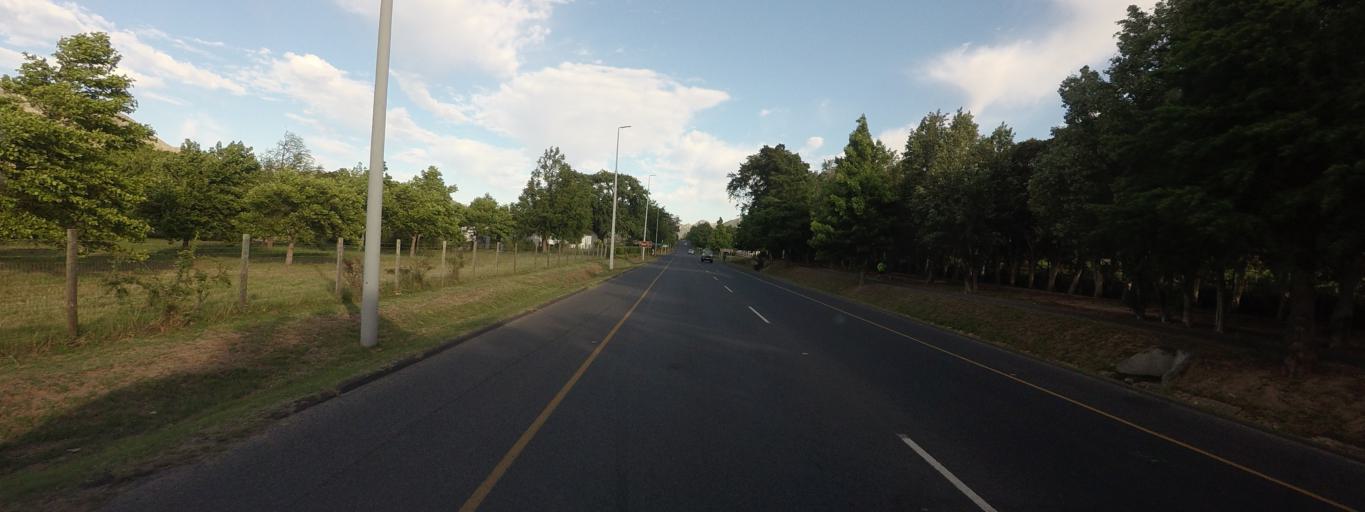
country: ZA
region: Western Cape
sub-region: Cape Winelands District Municipality
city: Paarl
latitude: -33.9024
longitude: 19.1085
